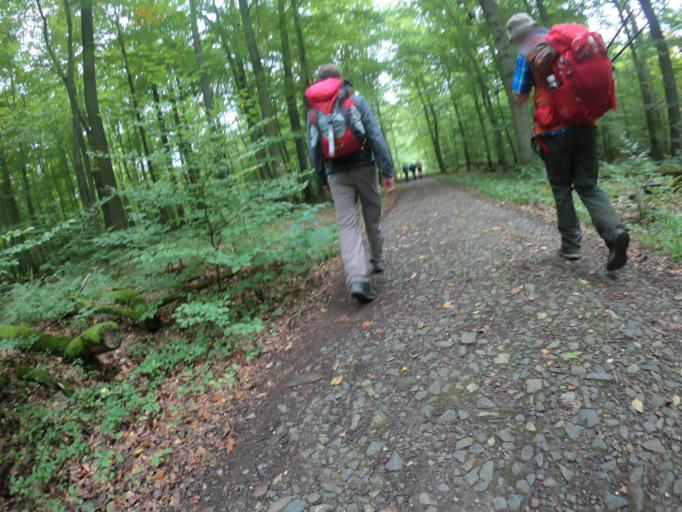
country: DE
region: Hesse
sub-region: Regierungsbezirk Darmstadt
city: Wiesbaden
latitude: 50.1130
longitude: 8.2476
